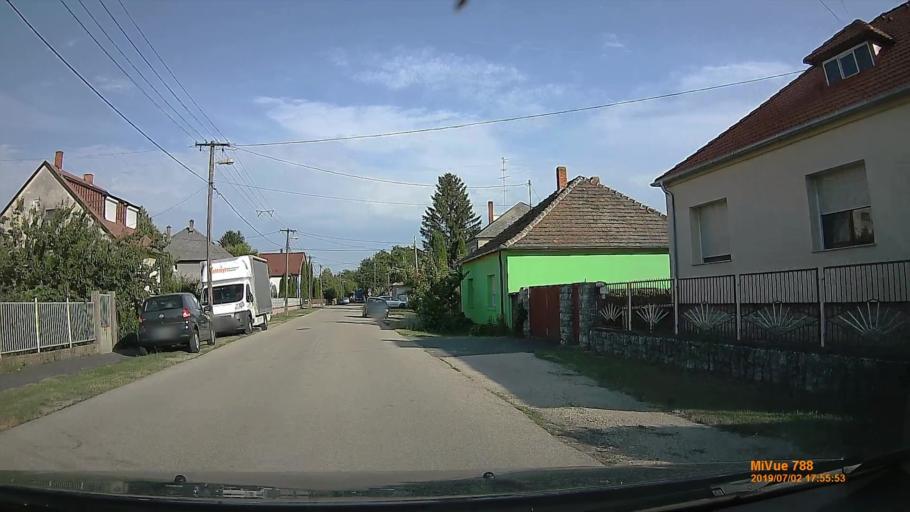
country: HU
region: Gyor-Moson-Sopron
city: Mosonmagyarovar
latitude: 47.8486
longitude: 17.2734
